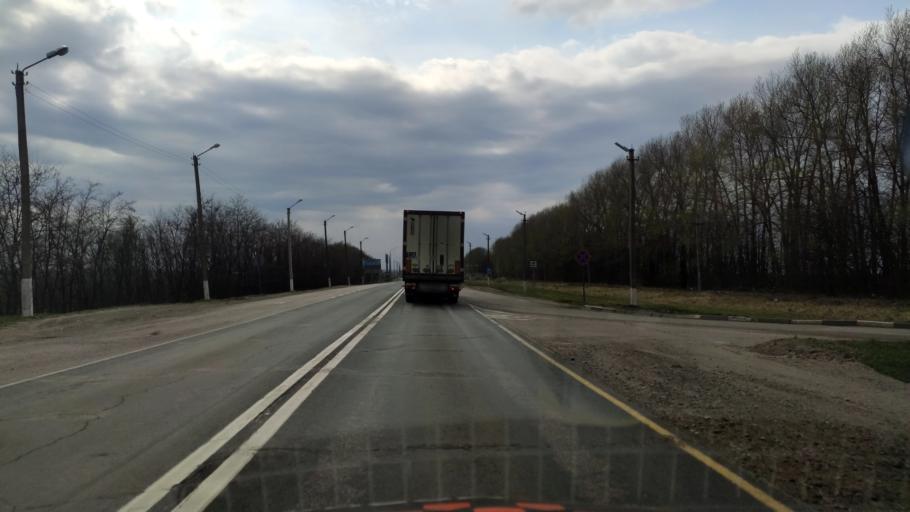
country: RU
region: Voronezj
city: Nizhnedevitsk
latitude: 51.5616
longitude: 38.2524
